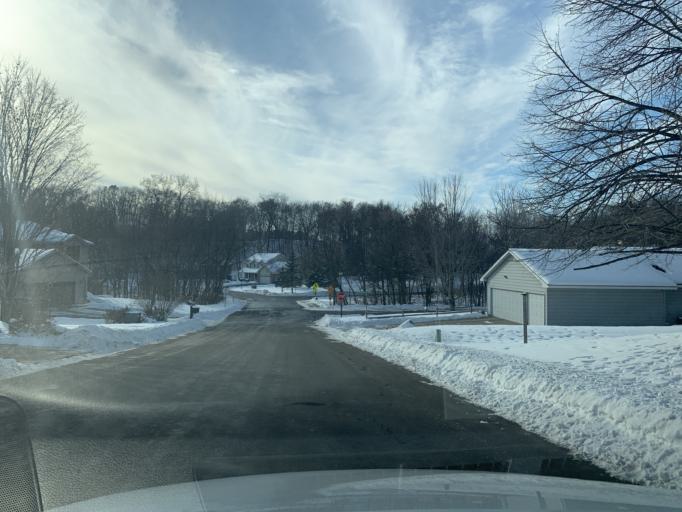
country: US
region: Minnesota
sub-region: Wright County
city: Saint Michael
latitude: 45.2047
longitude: -93.6566
